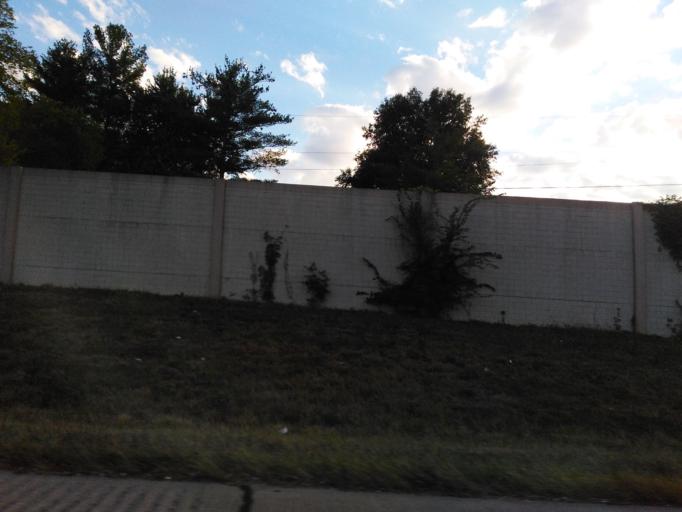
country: US
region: Missouri
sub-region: Saint Louis County
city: Sappington
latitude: 38.5179
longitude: -90.3887
